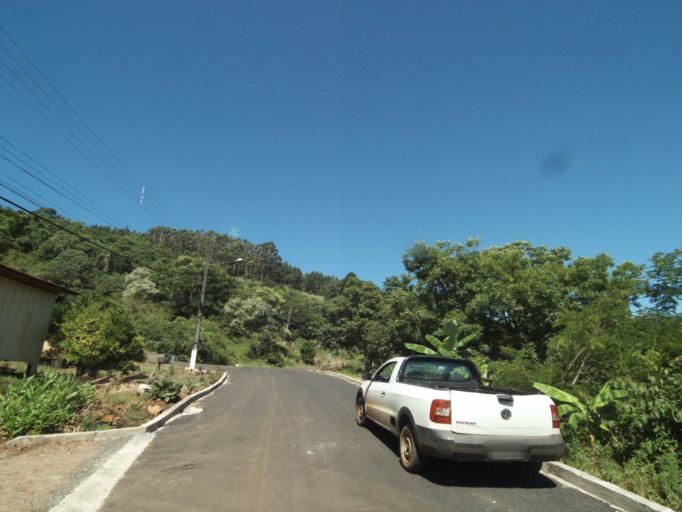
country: BR
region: Parana
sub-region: Ampere
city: Ampere
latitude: -26.1734
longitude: -53.3559
